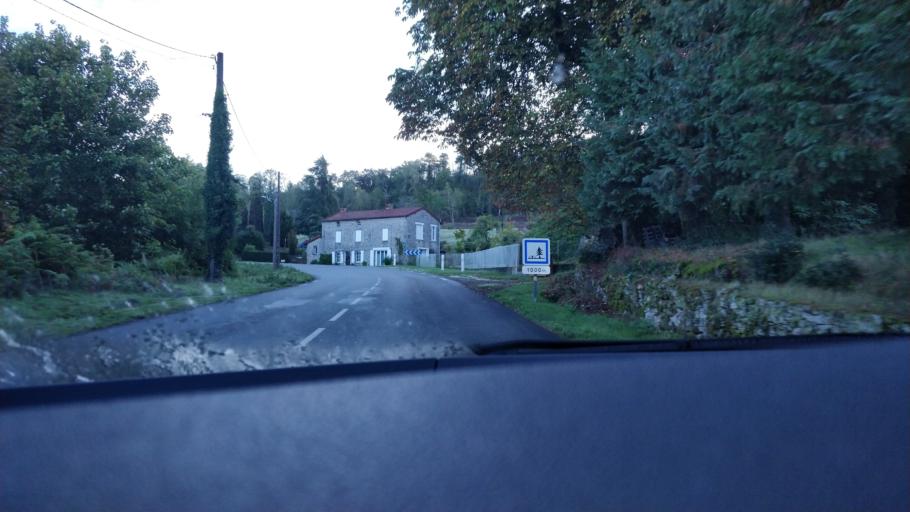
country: FR
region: Limousin
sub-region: Departement de la Haute-Vienne
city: Sauviat-sur-Vige
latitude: 45.9198
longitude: 1.6392
